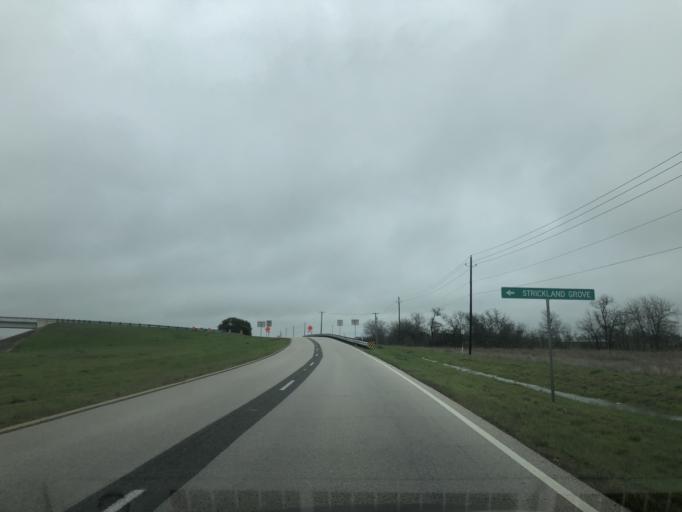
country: US
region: Texas
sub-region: Williamson County
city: Serenada
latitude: 30.7344
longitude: -97.6396
